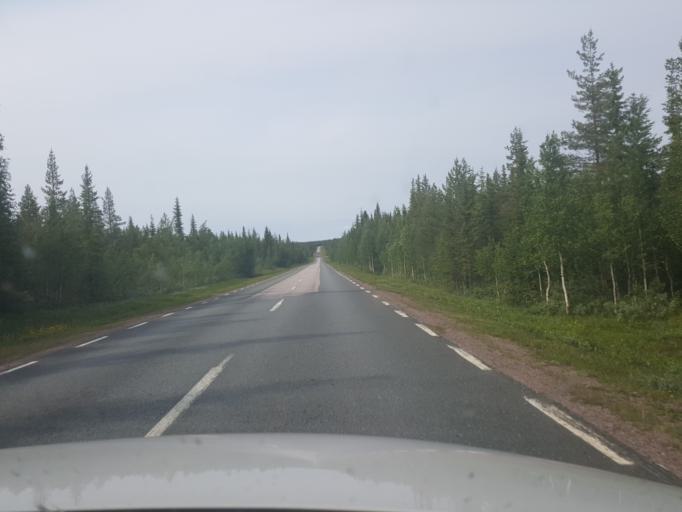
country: SE
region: Norrbotten
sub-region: Arjeplogs Kommun
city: Arjeplog
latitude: 65.7884
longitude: 18.0070
